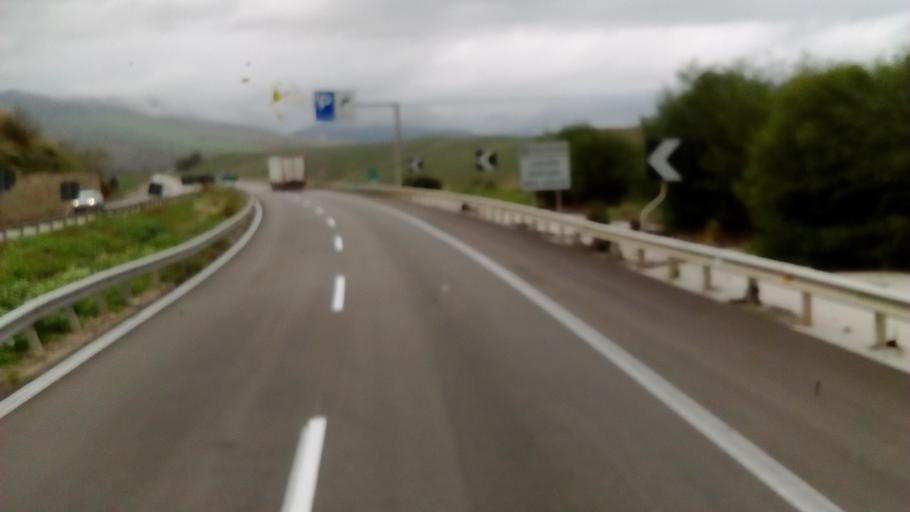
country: IT
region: Sicily
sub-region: Enna
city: Calascibetta
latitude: 37.5787
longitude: 14.2393
